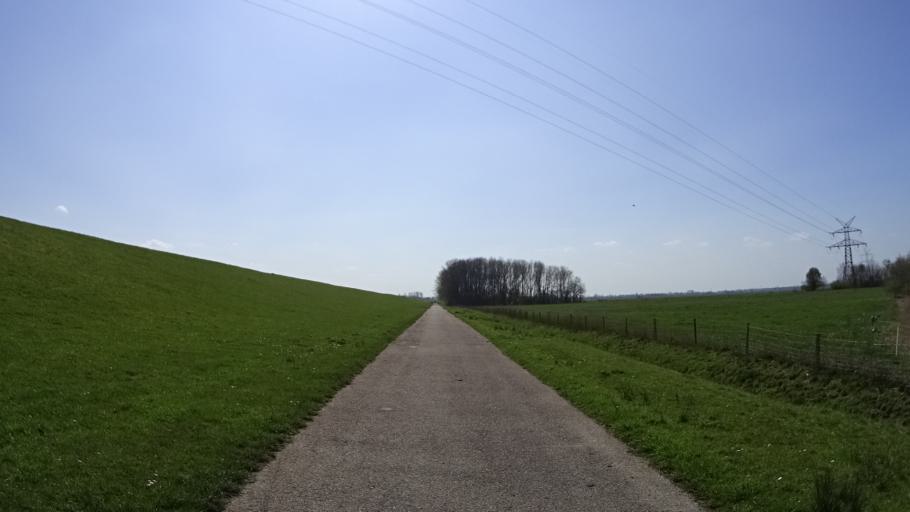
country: DE
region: Lower Saxony
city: Weener
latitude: 53.1483
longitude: 7.3704
